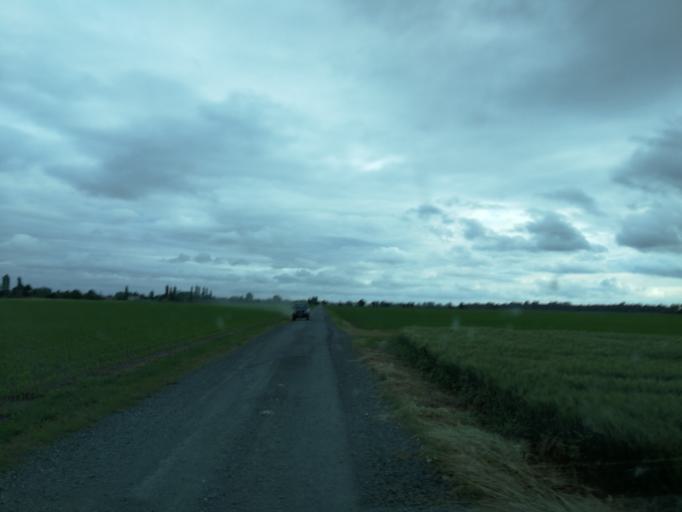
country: FR
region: Pays de la Loire
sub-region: Departement de la Vendee
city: Vix
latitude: 46.3642
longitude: -0.9351
